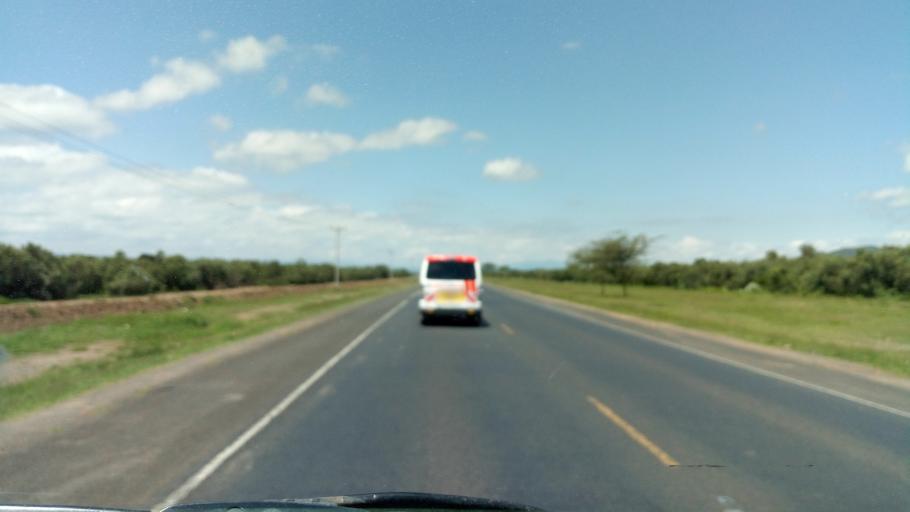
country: KE
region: Nakuru
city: Naivasha
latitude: -0.5550
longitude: 36.3499
